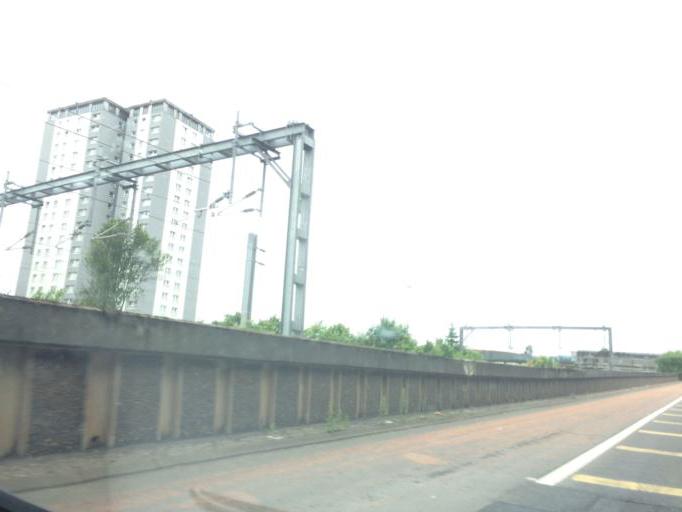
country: GB
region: Scotland
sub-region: Renfrewshire
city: Renfrew
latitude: 55.8531
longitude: -4.3418
